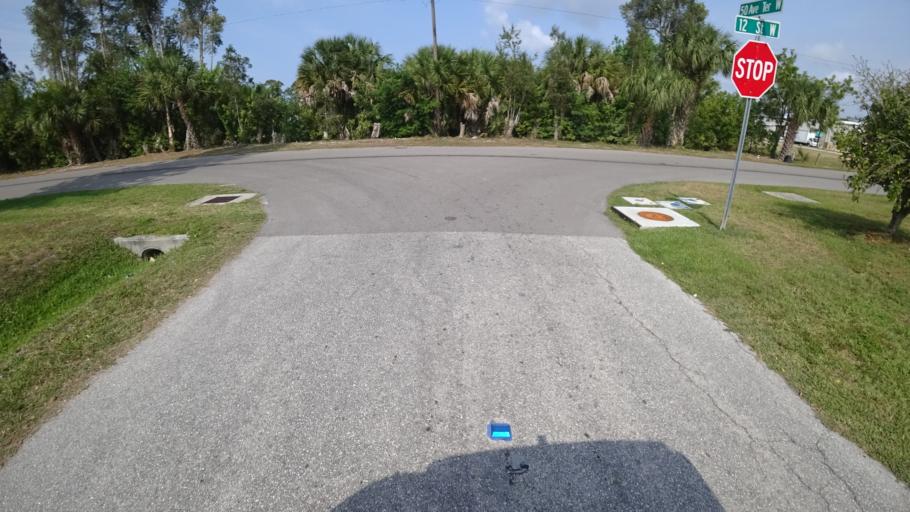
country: US
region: Florida
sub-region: Manatee County
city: South Bradenton
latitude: 27.4522
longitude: -82.5737
